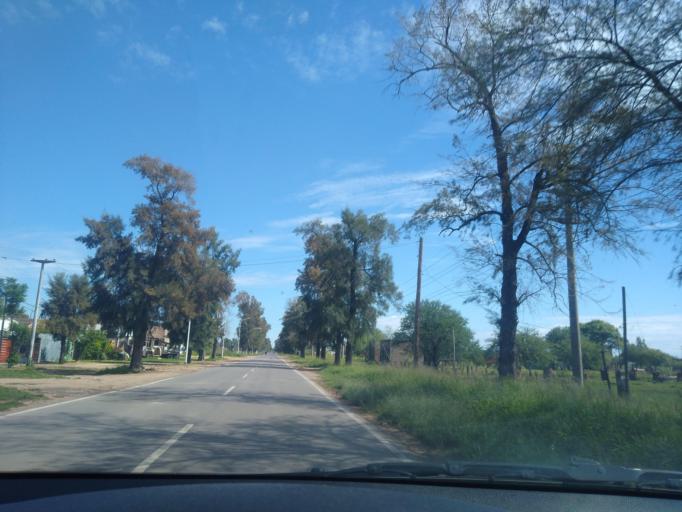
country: AR
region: Chaco
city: Presidencia Roque Saenz Pena
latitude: -26.7761
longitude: -60.4093
